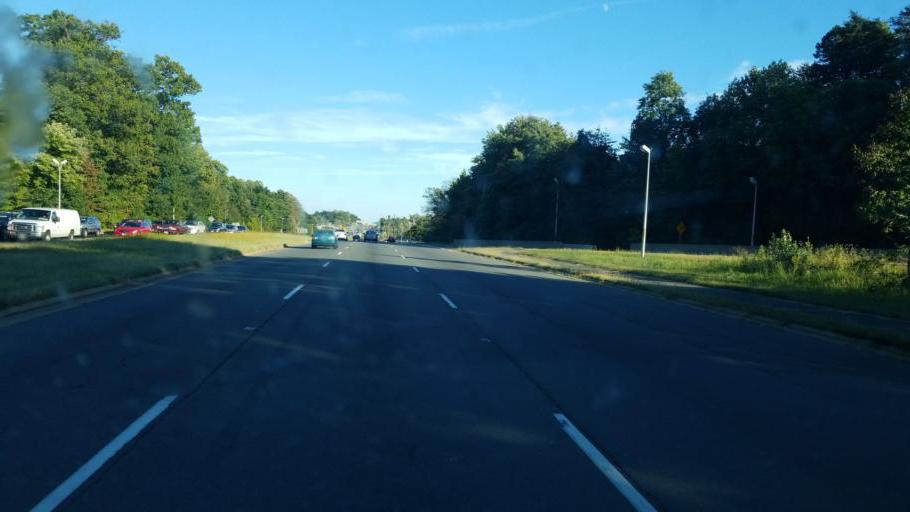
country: US
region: Virginia
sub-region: Fairfax County
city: Greenbriar
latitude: 38.8752
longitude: -77.3826
